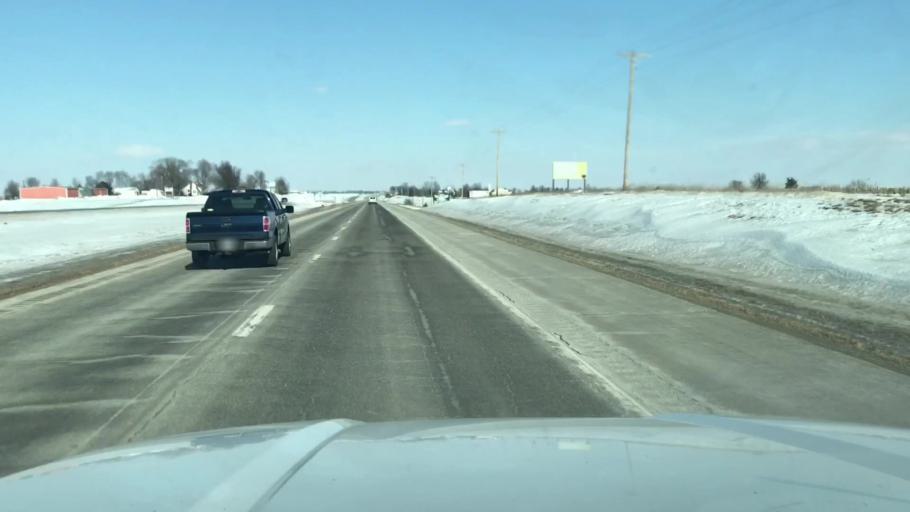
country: US
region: Missouri
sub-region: Nodaway County
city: Maryville
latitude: 40.2851
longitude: -94.8754
